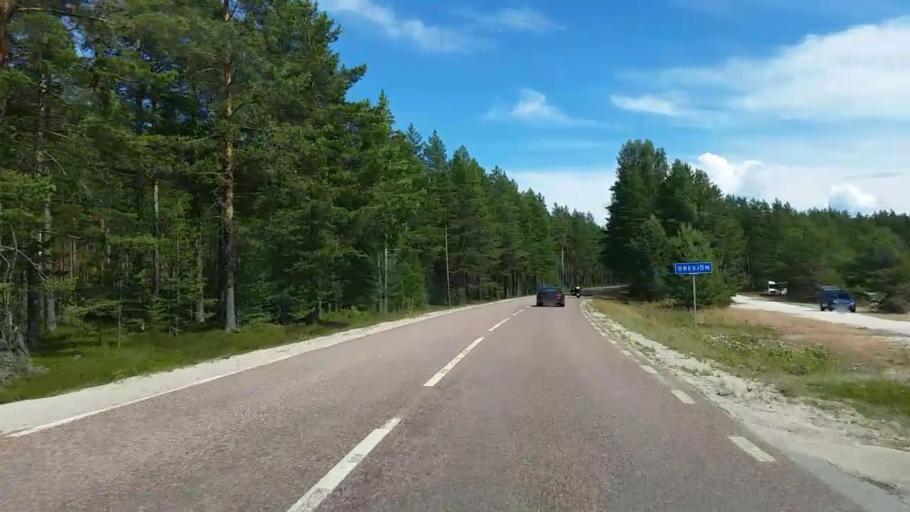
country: SE
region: Dalarna
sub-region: Rattviks Kommun
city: Raettvik
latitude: 61.1732
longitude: 15.1570
